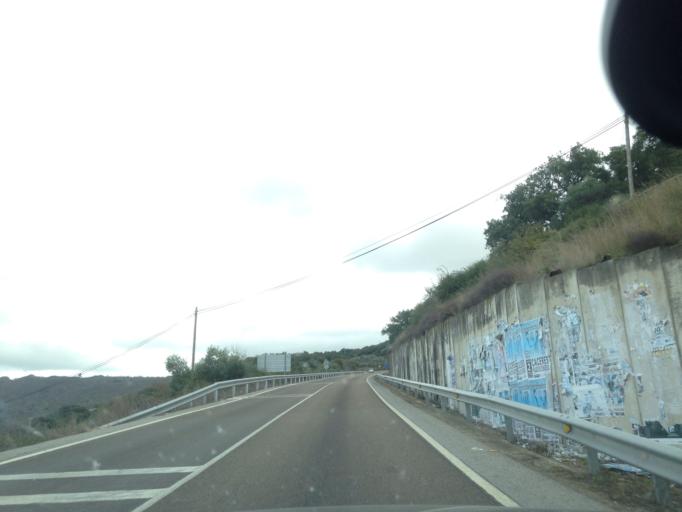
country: ES
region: Extremadura
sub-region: Provincia de Caceres
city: Montanchez
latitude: 39.2311
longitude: -6.1614
